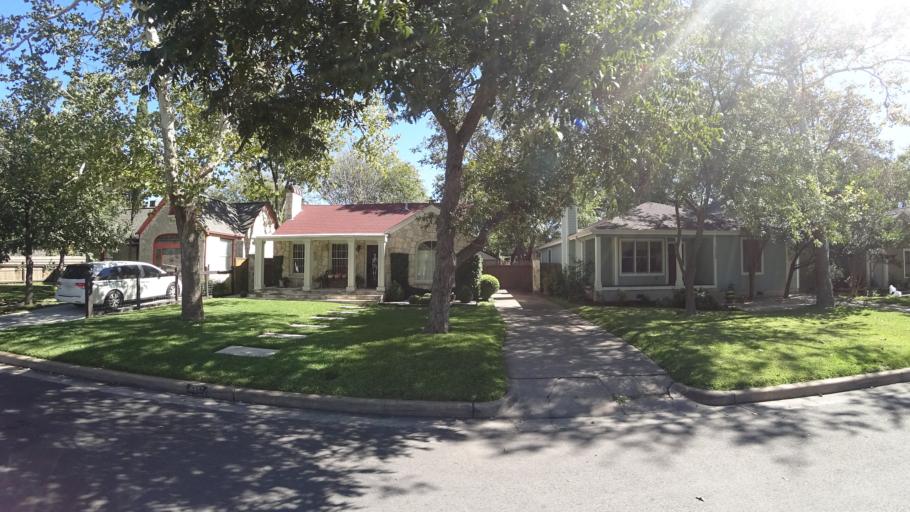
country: US
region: Texas
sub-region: Travis County
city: Austin
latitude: 30.3159
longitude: -97.7436
